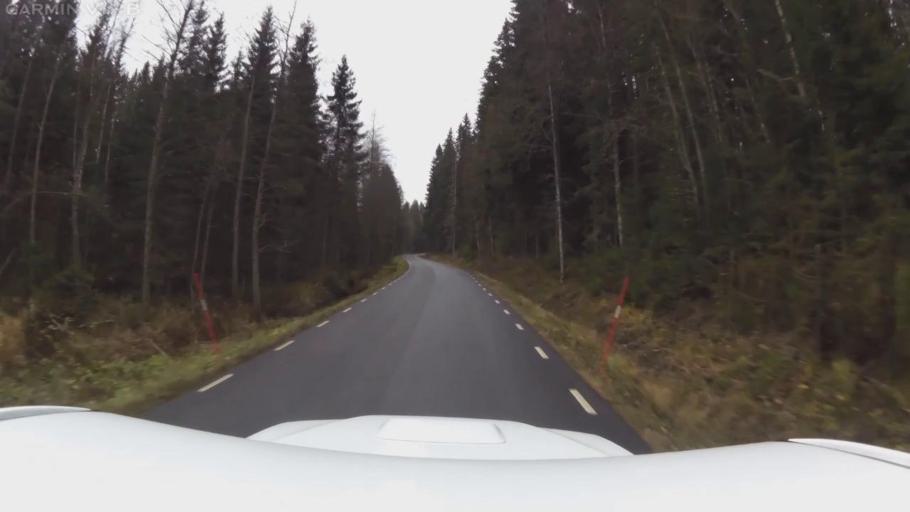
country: SE
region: OEstergoetland
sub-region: Mjolby Kommun
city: Mantorp
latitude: 58.1704
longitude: 15.3976
